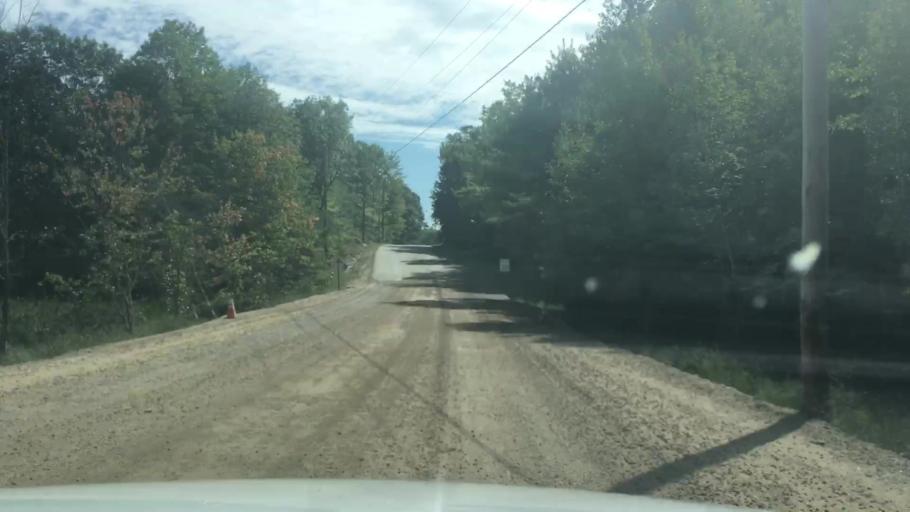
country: US
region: Maine
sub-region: Androscoggin County
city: Turner
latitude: 44.1933
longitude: -70.2524
